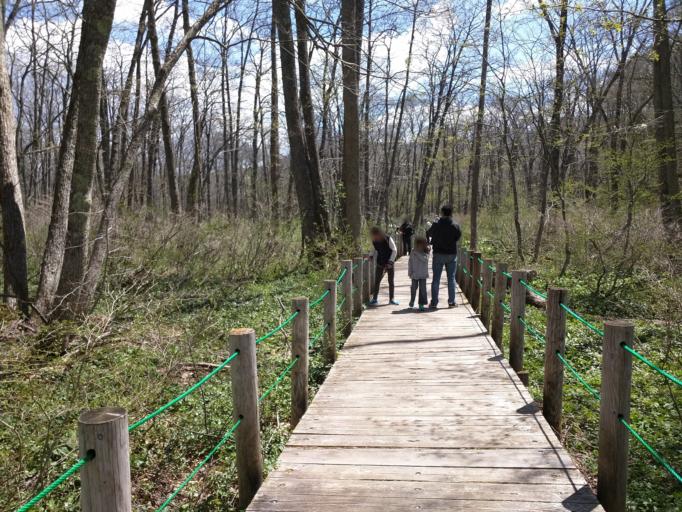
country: JP
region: Nagano
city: Nagano-shi
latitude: 36.7560
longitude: 138.0749
